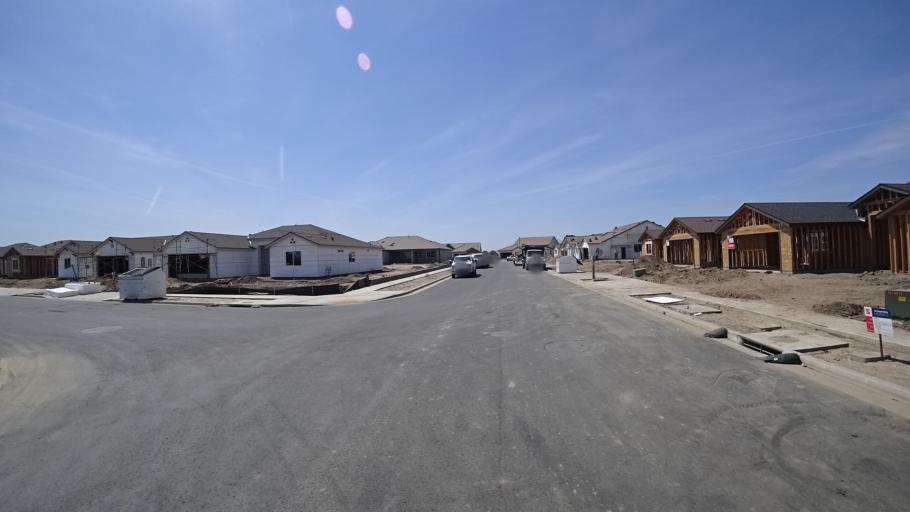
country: US
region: California
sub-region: Kings County
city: Lucerne
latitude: 36.3531
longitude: -119.6860
